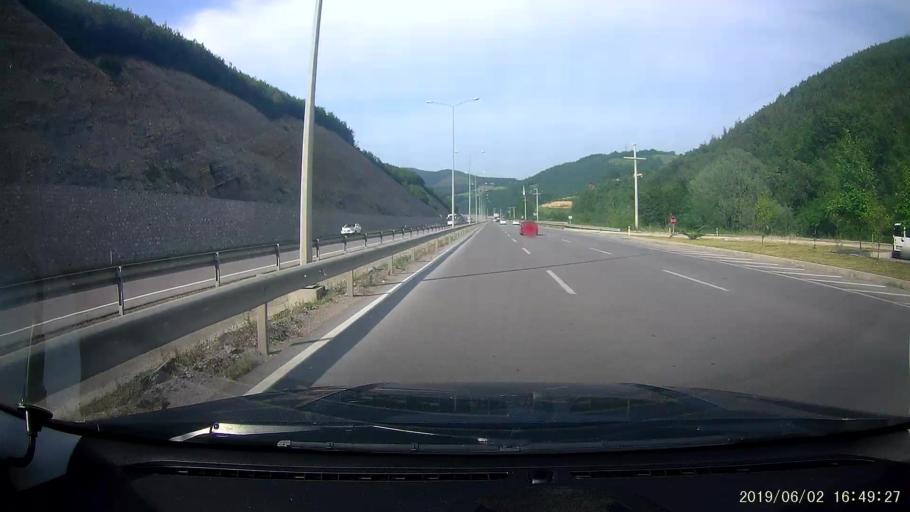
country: TR
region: Samsun
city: Samsun
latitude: 41.2379
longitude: 36.1622
